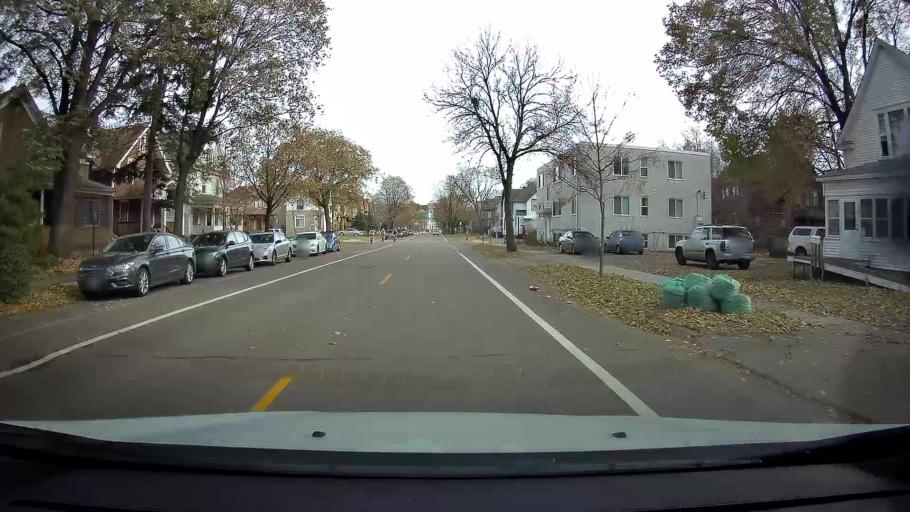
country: US
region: Minnesota
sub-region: Hennepin County
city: Minneapolis
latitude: 44.9852
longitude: -93.2347
